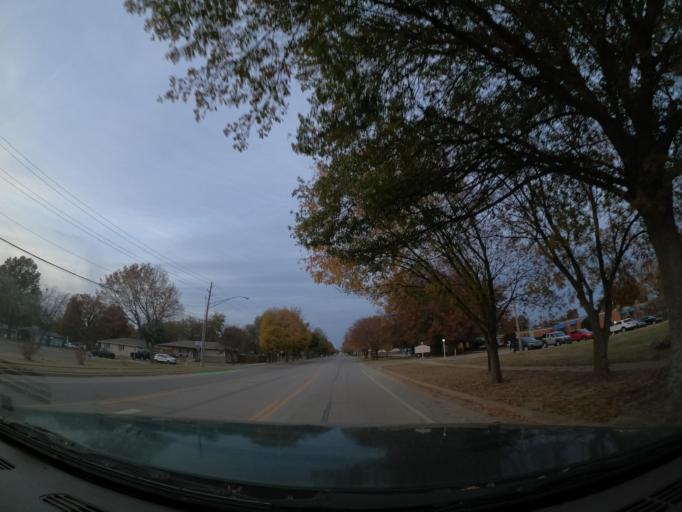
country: US
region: Oklahoma
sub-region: Tulsa County
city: Broken Arrow
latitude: 36.0338
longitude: -95.7908
